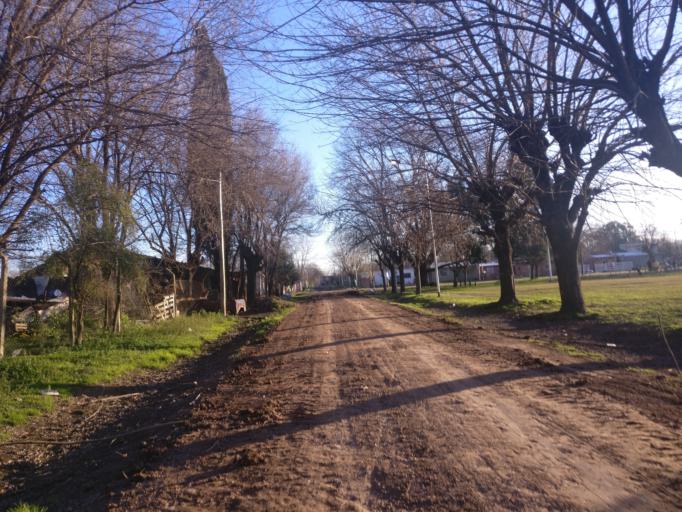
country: AR
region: Buenos Aires
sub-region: Partido de Ezeiza
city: Ezeiza
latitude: -34.9418
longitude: -58.6066
